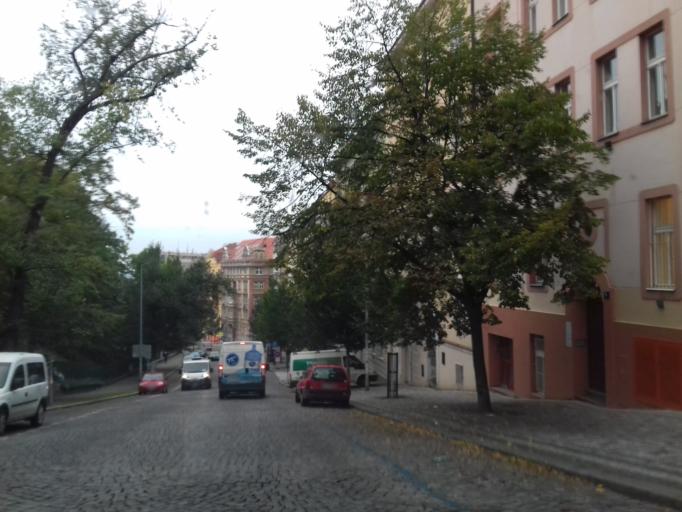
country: CZ
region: Praha
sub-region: Praha 8
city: Karlin
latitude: 50.0814
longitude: 14.4447
